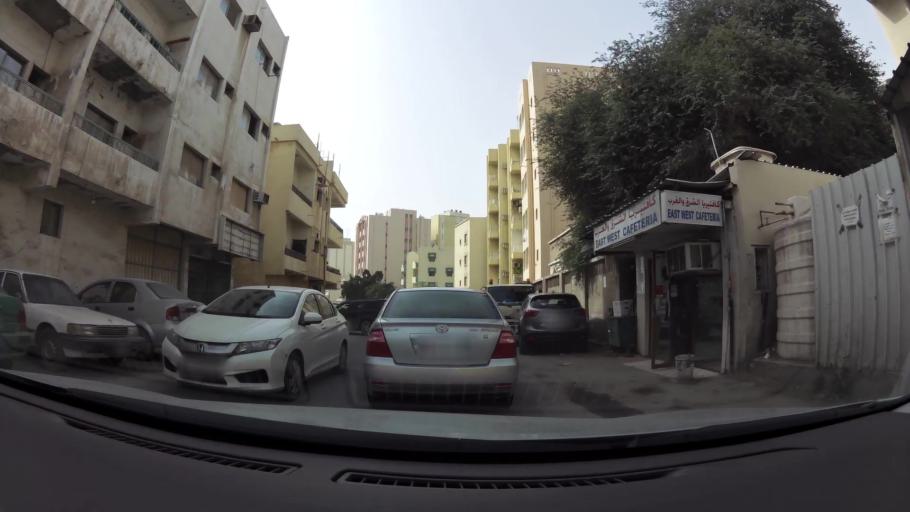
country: QA
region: Baladiyat ad Dawhah
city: Doha
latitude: 25.2770
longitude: 51.5499
